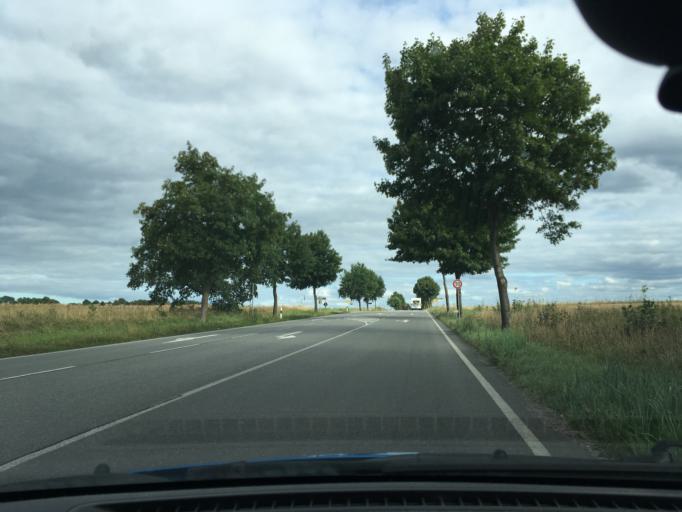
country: DE
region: Lower Saxony
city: Neu Wulmstorf
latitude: 53.4417
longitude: 9.7626
